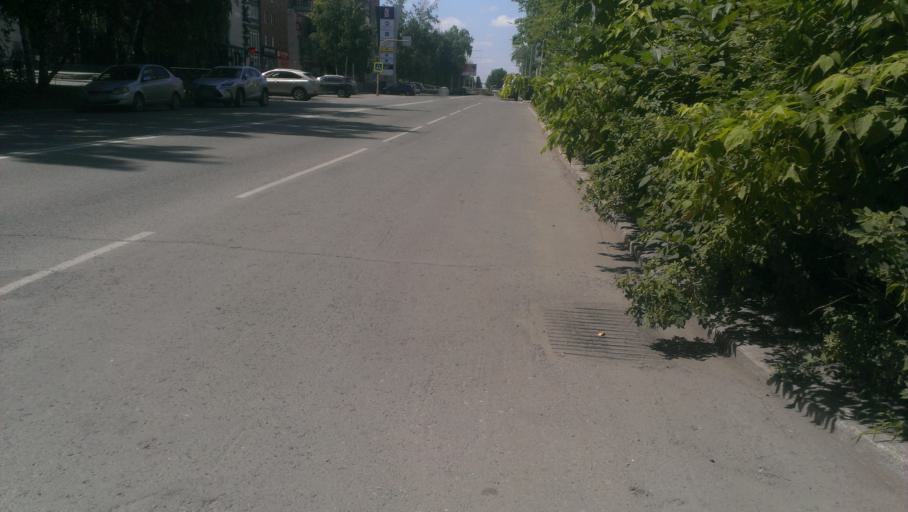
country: RU
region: Altai Krai
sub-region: Gorod Barnaulskiy
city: Barnaul
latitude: 53.3487
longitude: 83.7669
